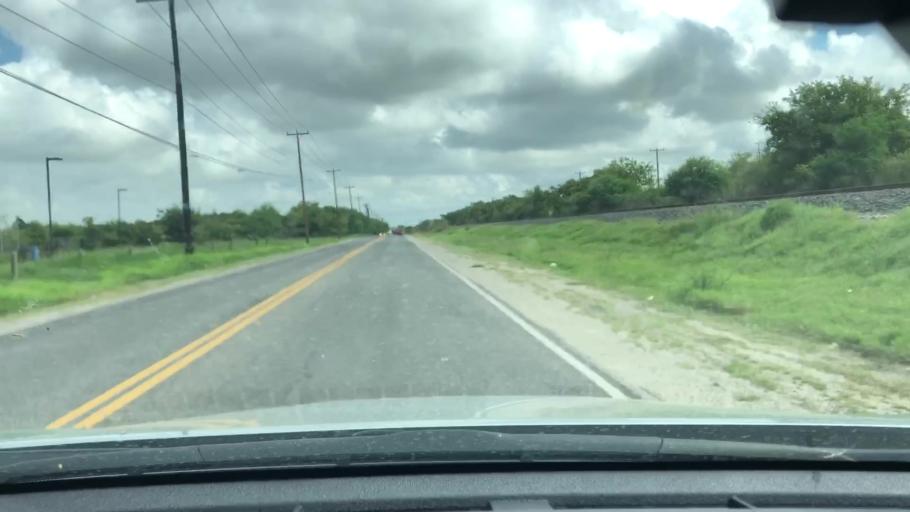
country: US
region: Texas
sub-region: Bexar County
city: Kirby
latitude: 29.4862
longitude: -98.3656
